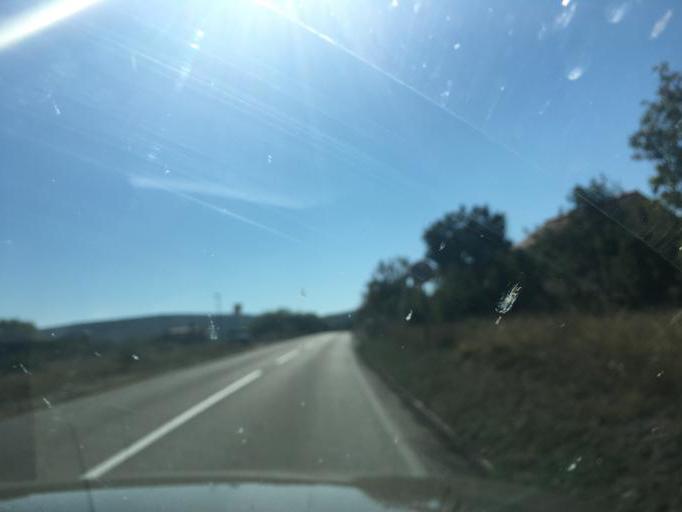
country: HR
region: Splitsko-Dalmatinska
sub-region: Grad Trogir
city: Trogir
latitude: 43.5868
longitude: 16.2307
